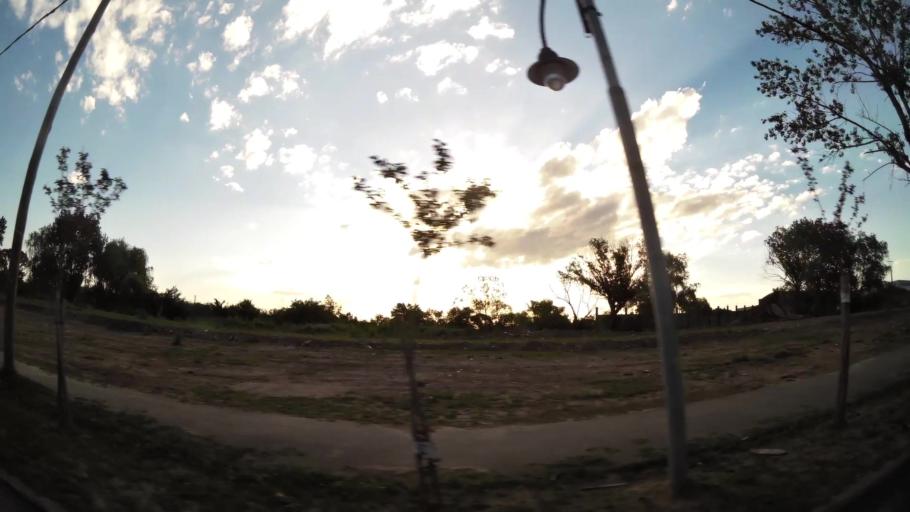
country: AR
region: Buenos Aires
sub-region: Partido de Tigre
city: Tigre
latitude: -34.4564
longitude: -58.5745
